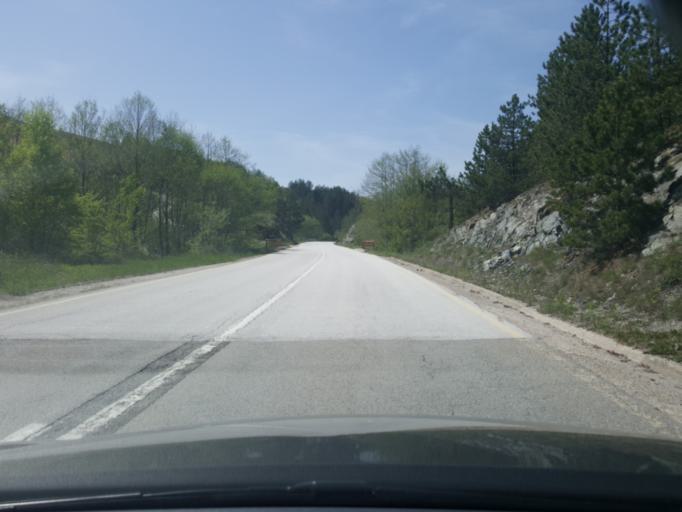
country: RS
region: Central Serbia
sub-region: Zlatiborski Okrug
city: Cajetina
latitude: 43.7903
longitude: 19.6608
